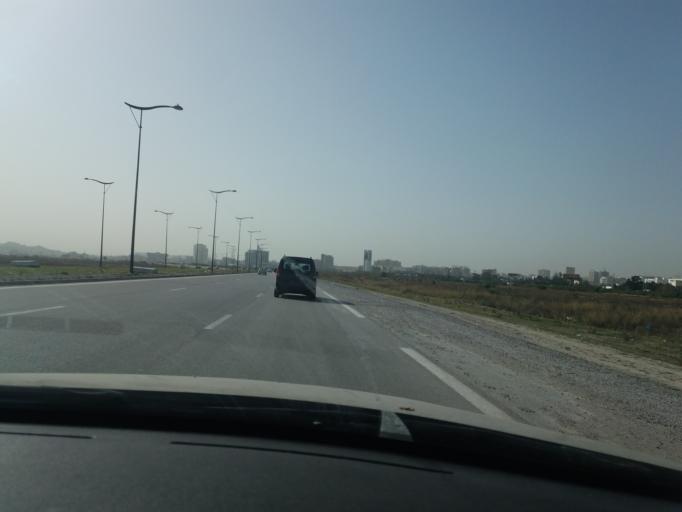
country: TN
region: Tunis
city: Tunis
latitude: 36.8193
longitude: 10.1982
